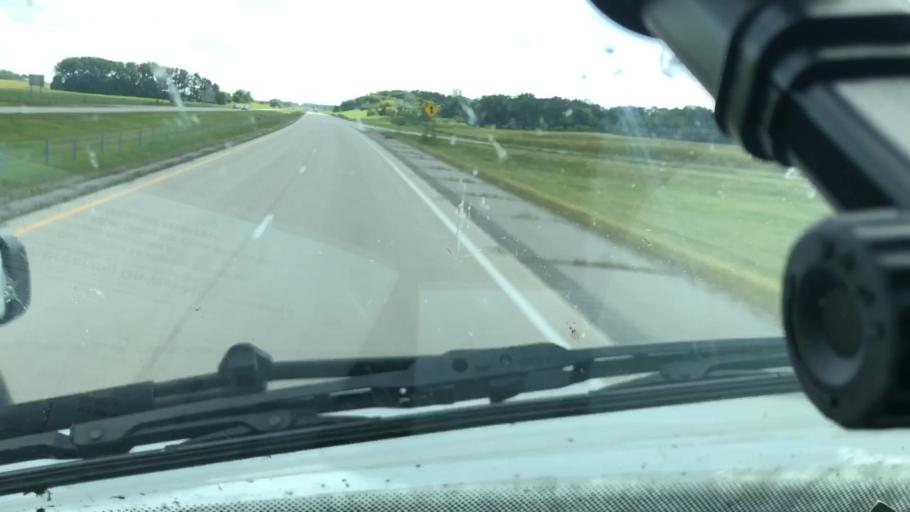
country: US
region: Minnesota
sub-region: Freeborn County
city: Albert Lea
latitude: 43.5735
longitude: -93.3594
